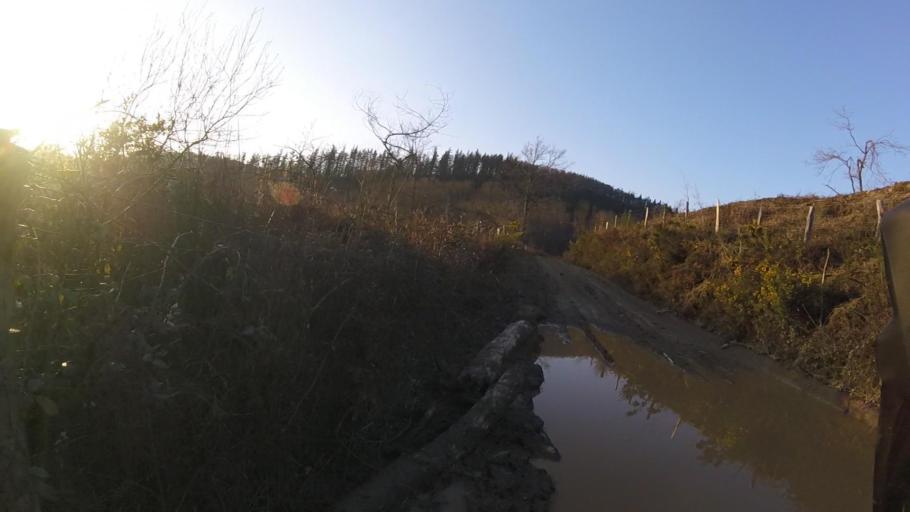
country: ES
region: Navarre
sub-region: Provincia de Navarra
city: Arano
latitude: 43.2502
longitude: -1.8611
